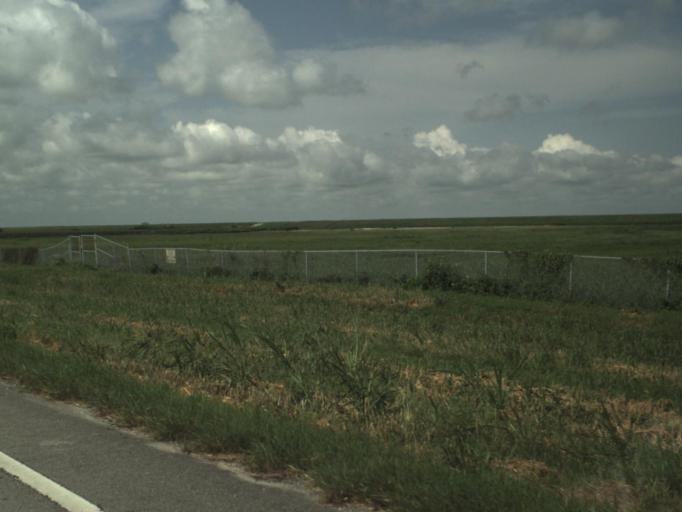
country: US
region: Florida
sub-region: Palm Beach County
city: Pahokee
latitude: 26.7834
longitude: -80.6893
